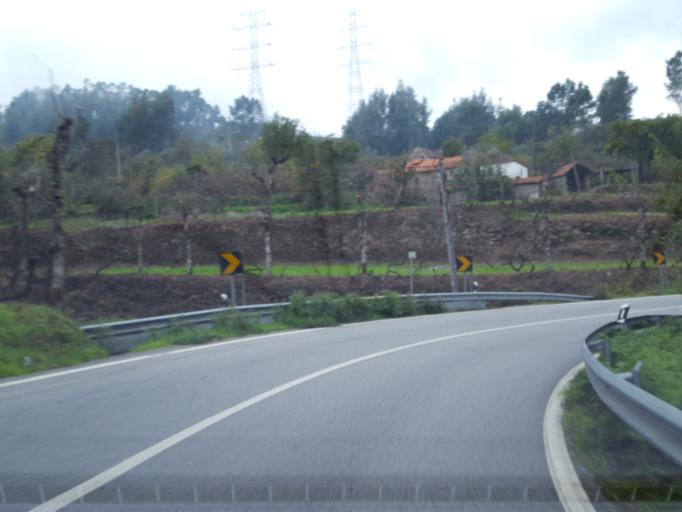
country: PT
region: Porto
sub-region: Marco de Canaveses
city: Marco de Canavezes
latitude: 41.1550
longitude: -8.1427
